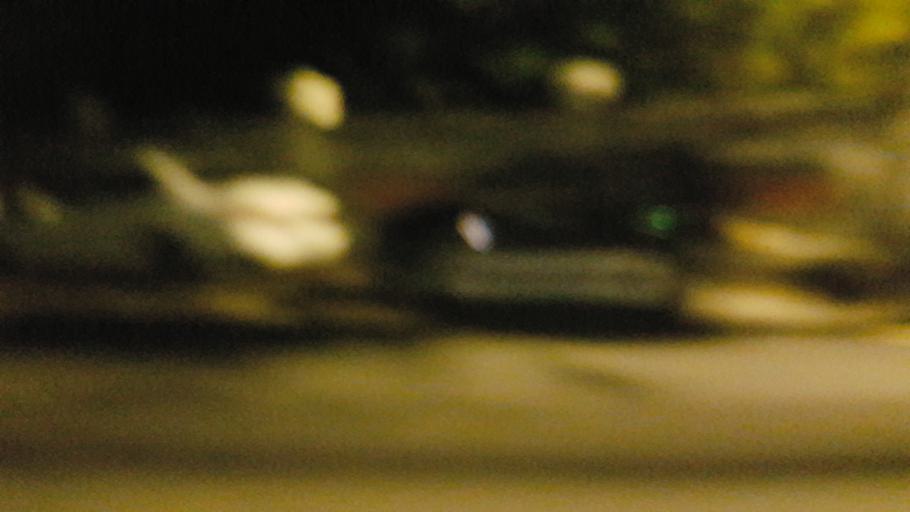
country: TW
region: Taiwan
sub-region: Hsinchu
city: Hsinchu
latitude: 24.7642
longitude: 120.9909
